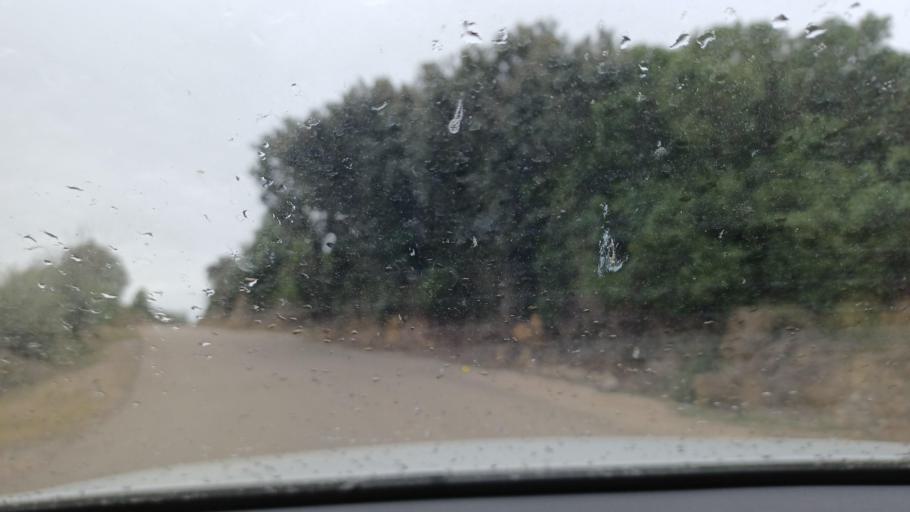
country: ES
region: Valencia
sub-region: Provincia de Castello
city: Traiguera
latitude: 40.5170
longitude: 0.2915
